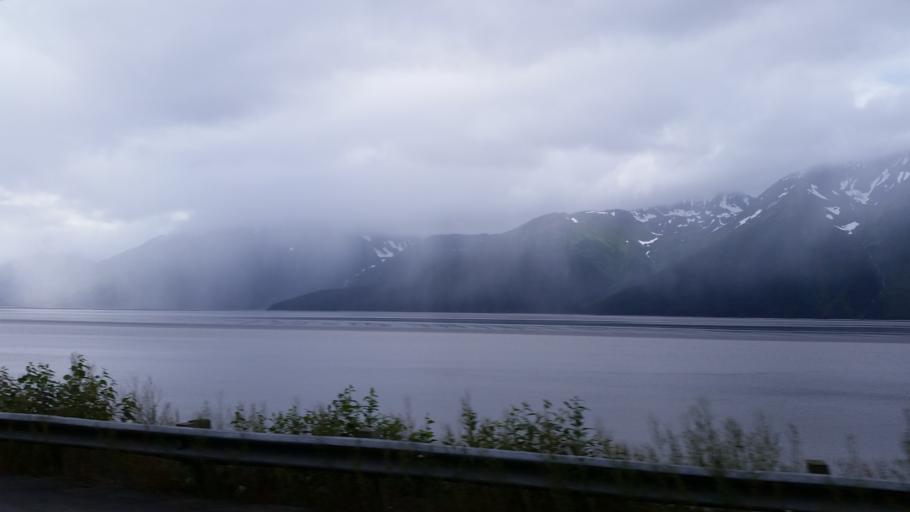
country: US
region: Alaska
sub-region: Anchorage Municipality
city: Girdwood
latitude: 60.9347
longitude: -149.3102
